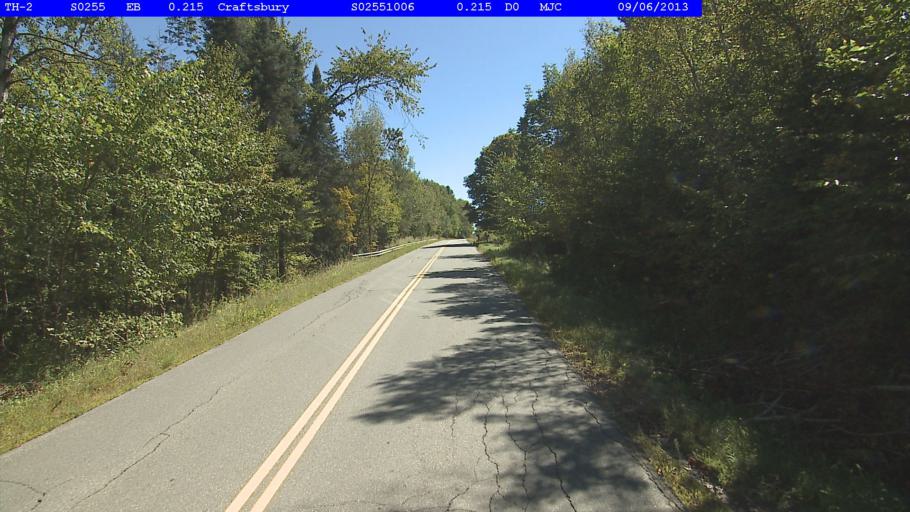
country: US
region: Vermont
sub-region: Caledonia County
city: Hardwick
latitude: 44.6282
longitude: -72.3599
